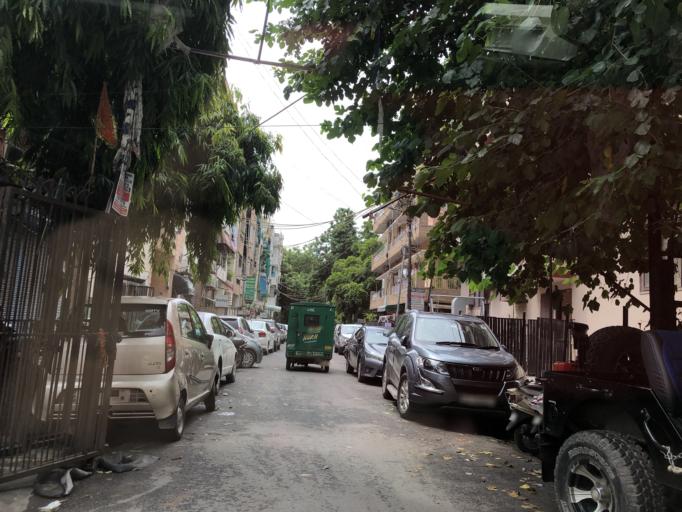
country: IN
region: NCT
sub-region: New Delhi
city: New Delhi
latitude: 28.5743
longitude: 77.2410
